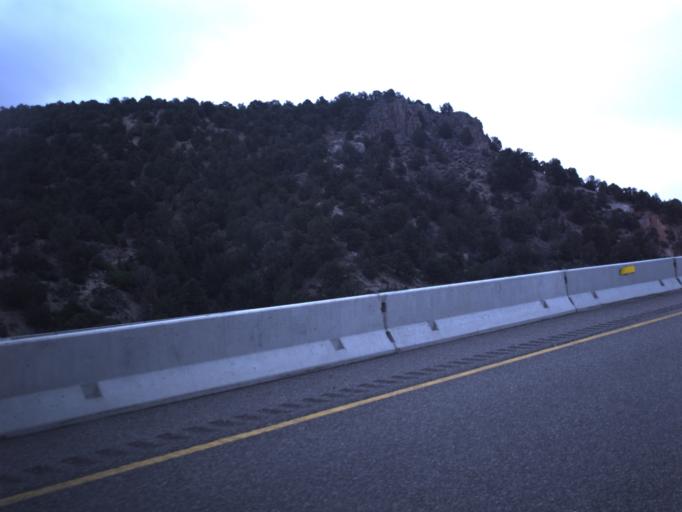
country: US
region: Utah
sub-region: Sevier County
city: Monroe
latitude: 38.5619
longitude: -112.4279
